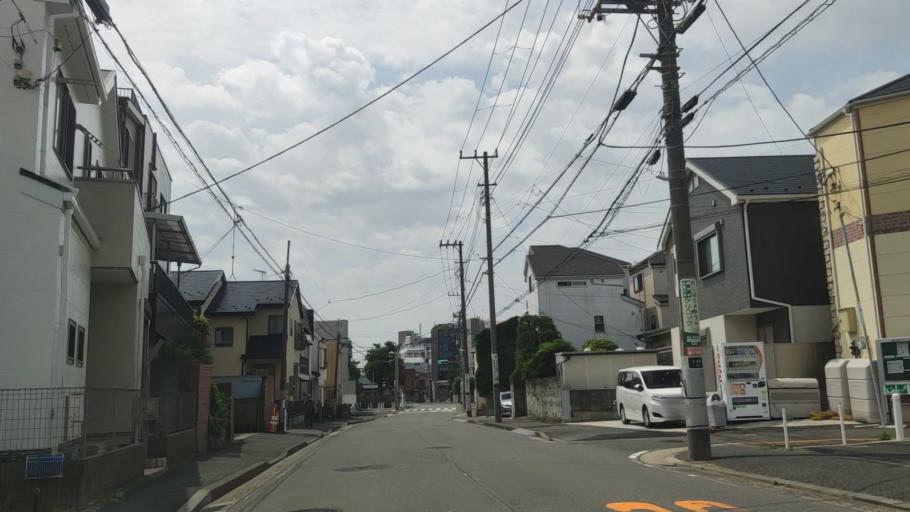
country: JP
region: Kanagawa
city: Yokohama
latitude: 35.4155
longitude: 139.6239
